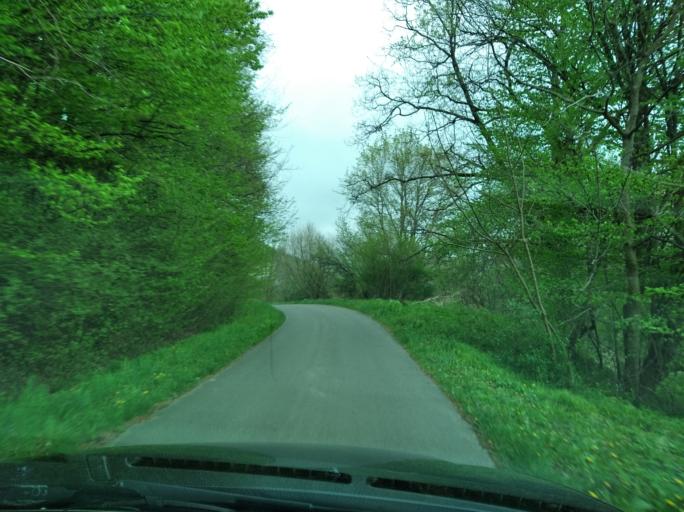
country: PL
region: Subcarpathian Voivodeship
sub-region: Powiat brzozowski
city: Dydnia
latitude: 49.6599
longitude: 22.2603
